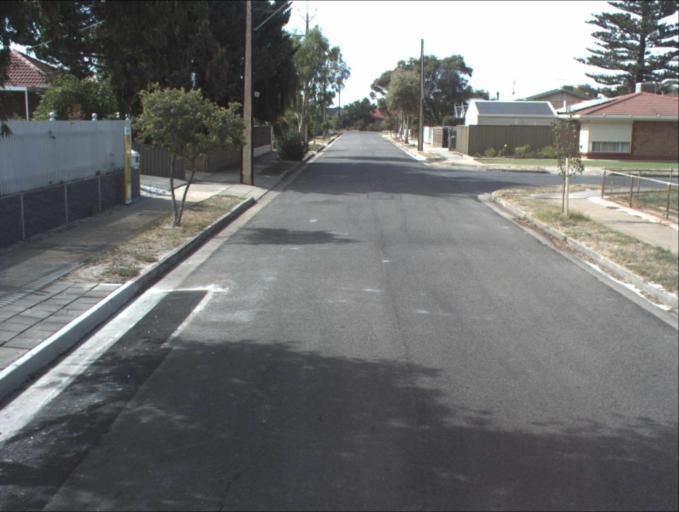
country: AU
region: South Australia
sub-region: Port Adelaide Enfield
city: Birkenhead
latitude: -34.7977
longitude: 138.4939
